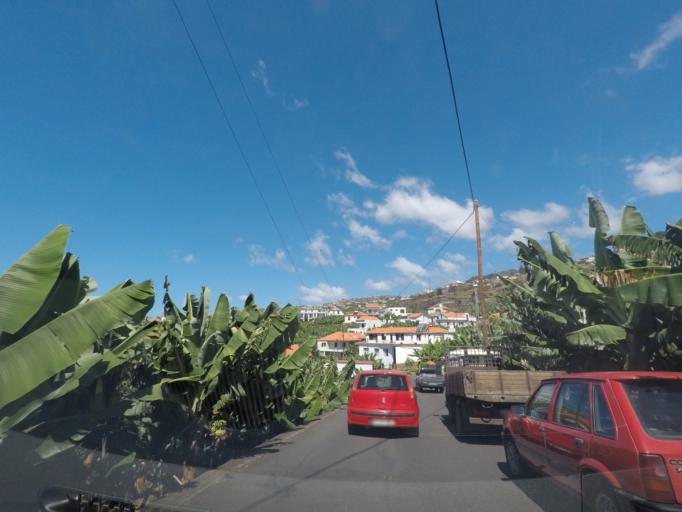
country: PT
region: Madeira
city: Ponta do Sol
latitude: 32.6861
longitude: -17.0936
